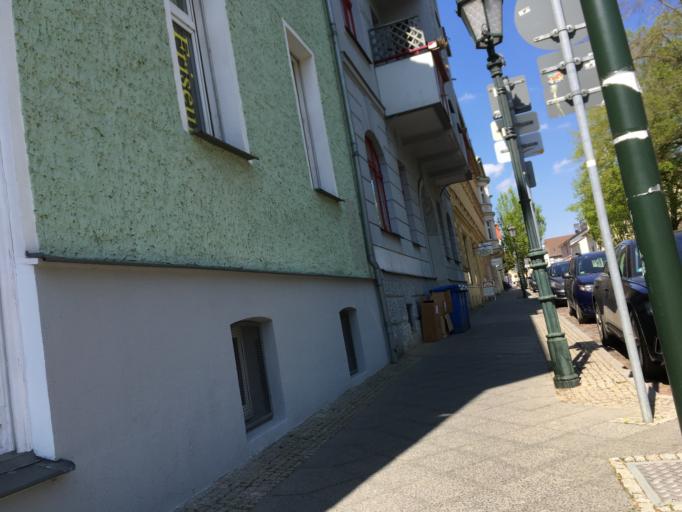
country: DE
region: Brandenburg
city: Bernau bei Berlin
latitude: 52.6767
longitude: 13.5904
